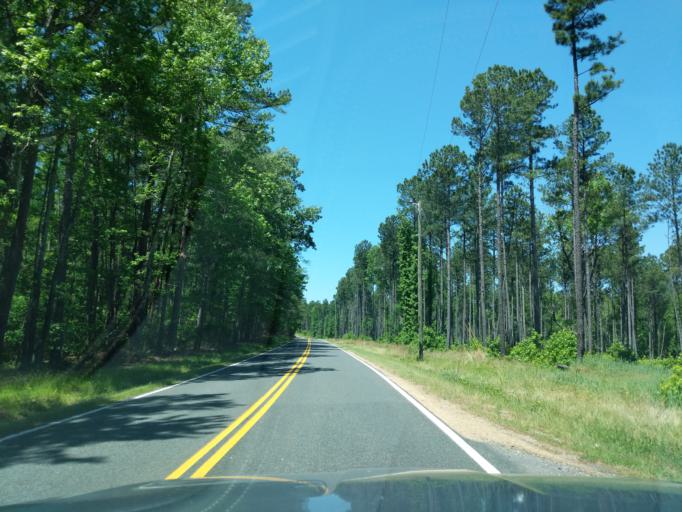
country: US
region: Georgia
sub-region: Columbia County
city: Evans
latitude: 33.6239
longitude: -82.1148
